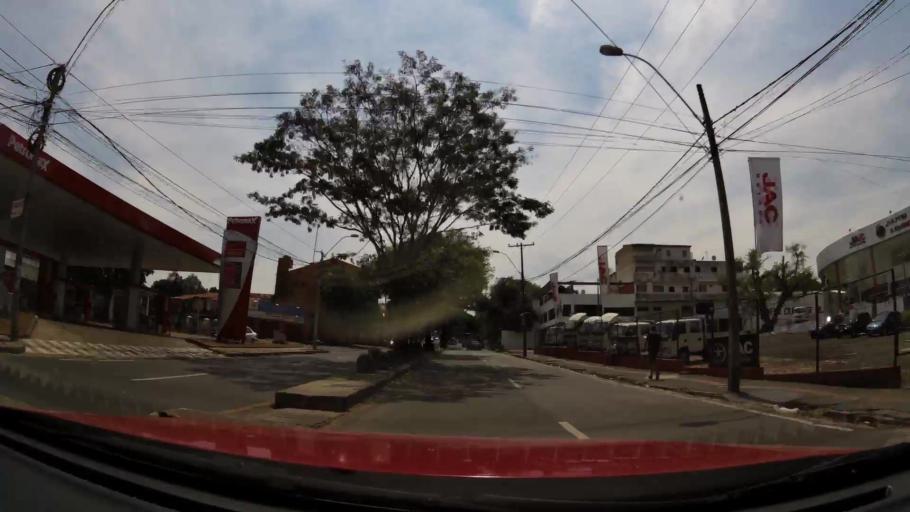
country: PY
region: Central
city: Lambare
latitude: -25.3231
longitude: -57.5953
